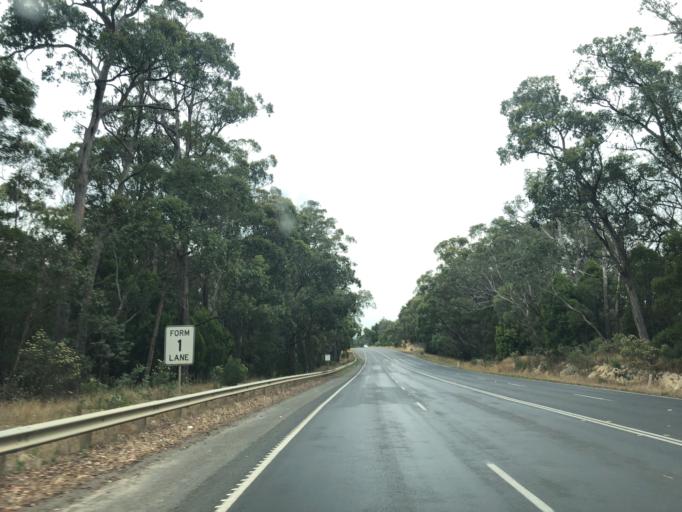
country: AU
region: Victoria
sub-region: Hume
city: Sunbury
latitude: -37.4054
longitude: 144.5379
